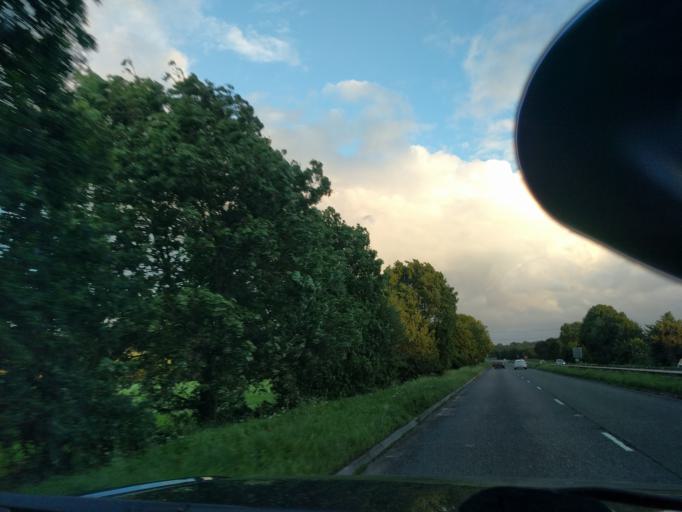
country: GB
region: England
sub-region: Wiltshire
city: Chippenham
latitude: 51.4845
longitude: -2.1285
